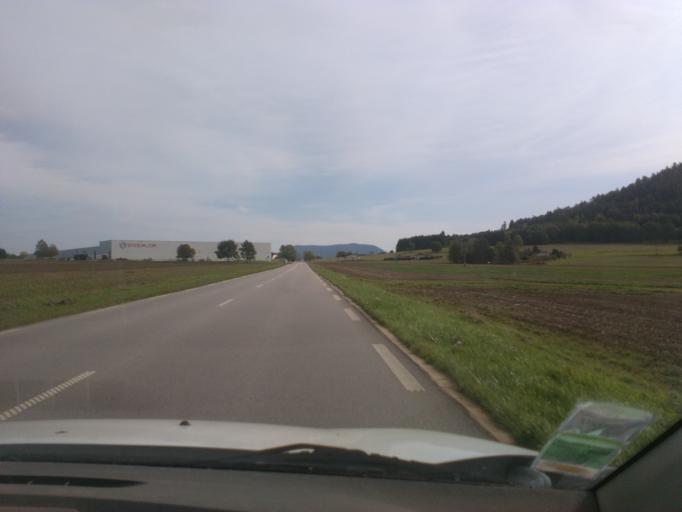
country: FR
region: Lorraine
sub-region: Departement des Vosges
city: Etival-Clairefontaine
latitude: 48.3218
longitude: 6.8383
